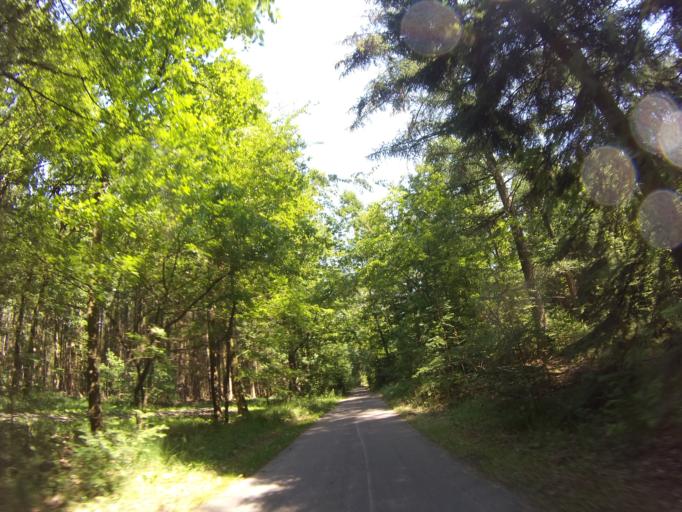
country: NL
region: Drenthe
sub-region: Gemeente Coevorden
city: Sleen
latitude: 52.8319
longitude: 6.7369
